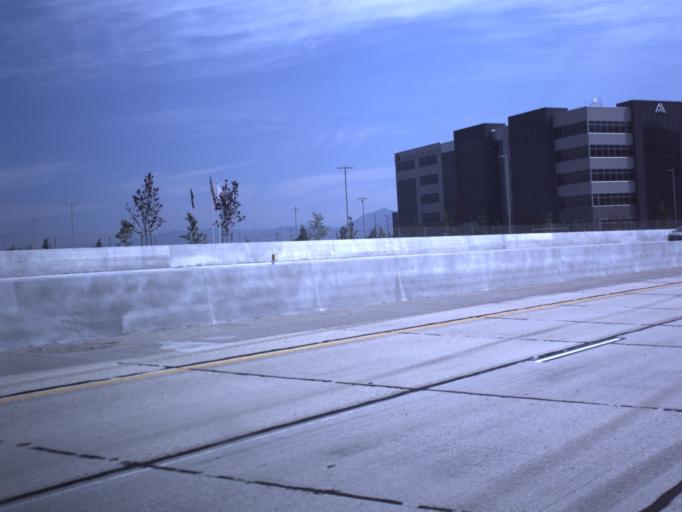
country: US
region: Utah
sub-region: Salt Lake County
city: Bluffdale
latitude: 40.5035
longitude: -111.9030
